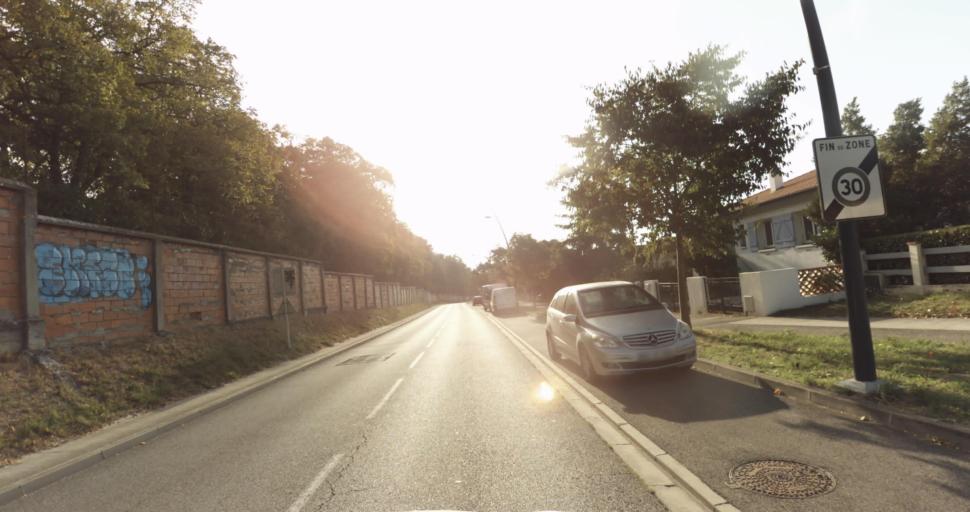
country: FR
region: Midi-Pyrenees
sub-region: Departement de la Haute-Garonne
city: Ramonville-Saint-Agne
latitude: 43.5393
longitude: 1.4644
